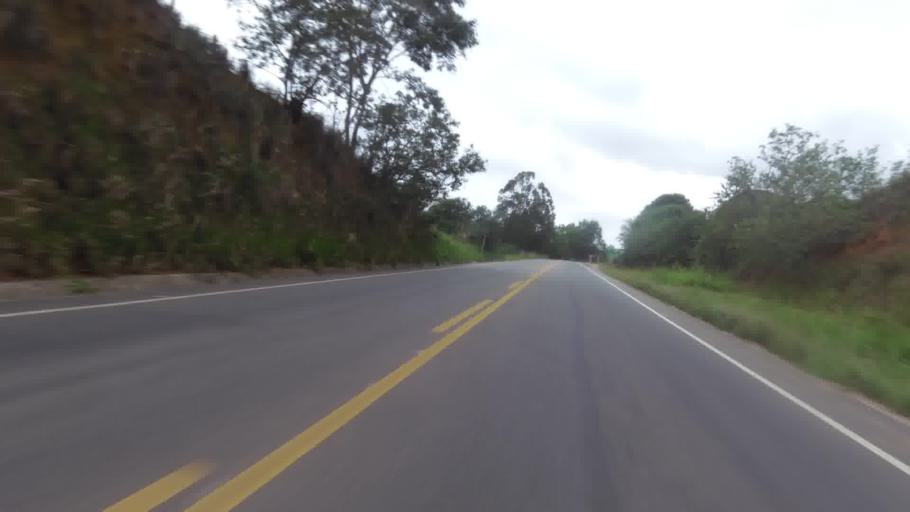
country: BR
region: Espirito Santo
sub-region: Iconha
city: Iconha
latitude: -20.7813
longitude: -40.7563
